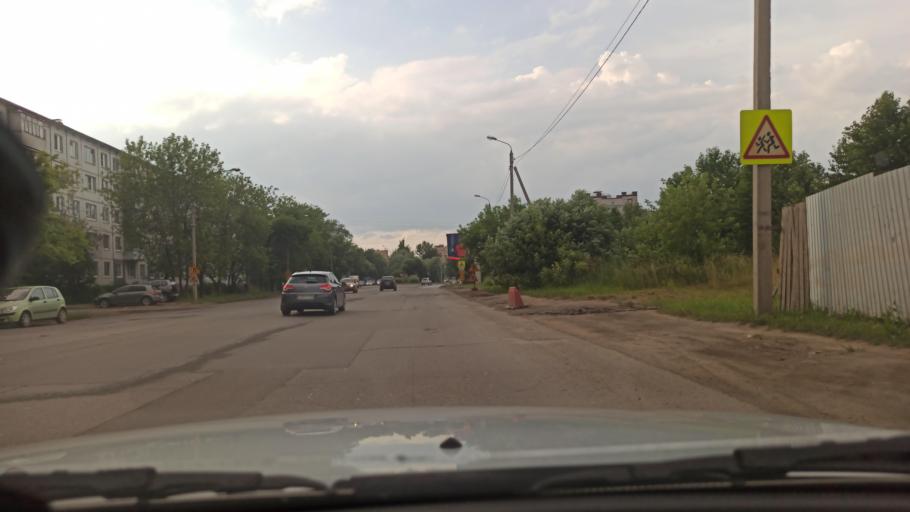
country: RU
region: Vologda
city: Vologda
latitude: 59.2049
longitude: 39.8510
